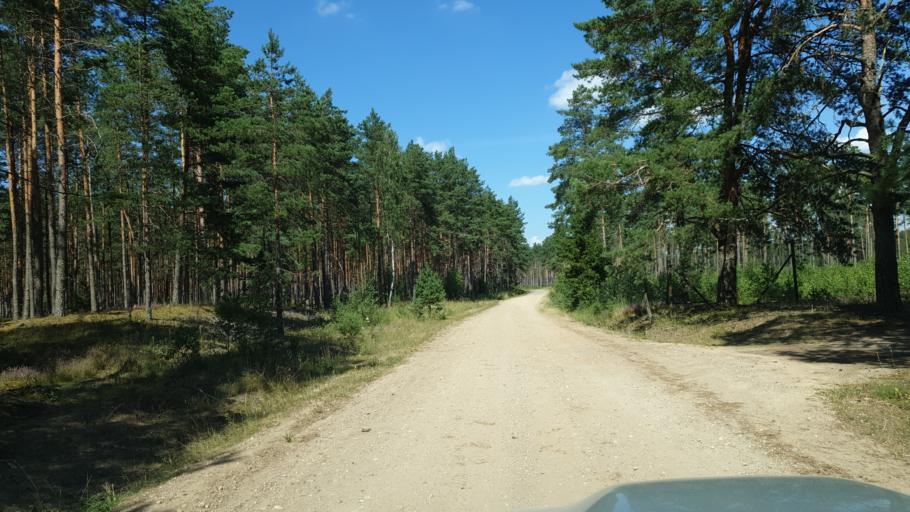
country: LT
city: Sirvintos
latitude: 54.8954
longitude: 24.9572
